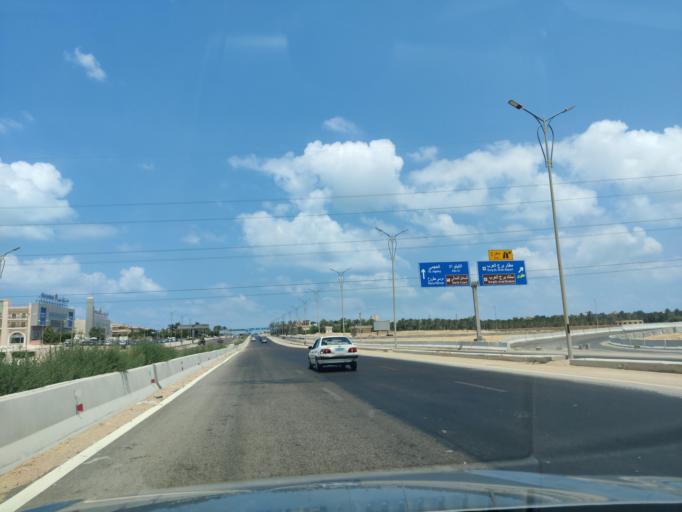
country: EG
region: Alexandria
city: Alexandria
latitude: 31.0044
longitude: 29.6407
